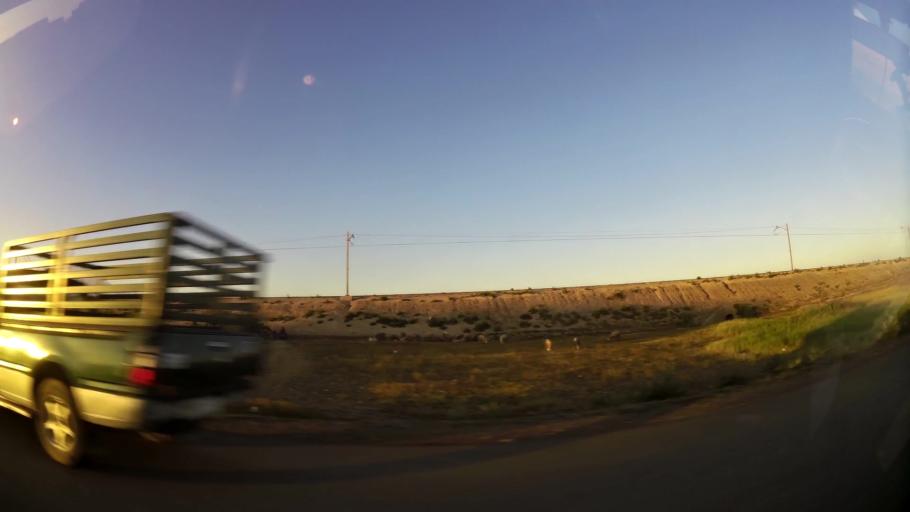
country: MA
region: Marrakech-Tensift-Al Haouz
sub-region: Kelaa-Des-Sraghna
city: Sidi Abdallah
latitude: 32.2395
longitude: -7.9300
